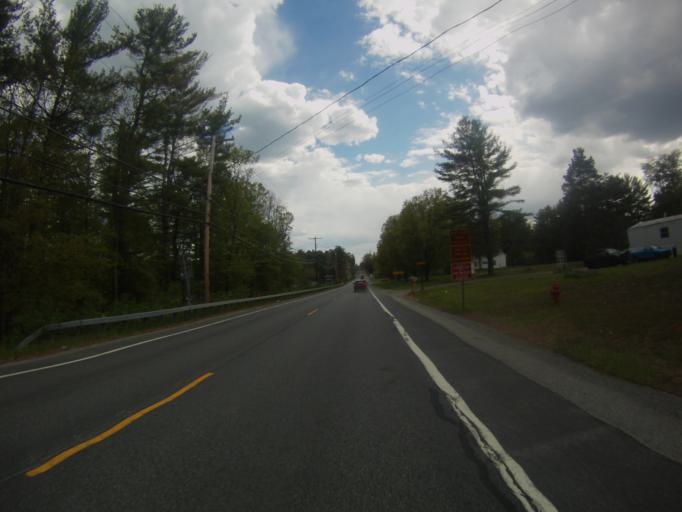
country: US
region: New York
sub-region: Essex County
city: Ticonderoga
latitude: 43.8484
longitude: -73.7581
